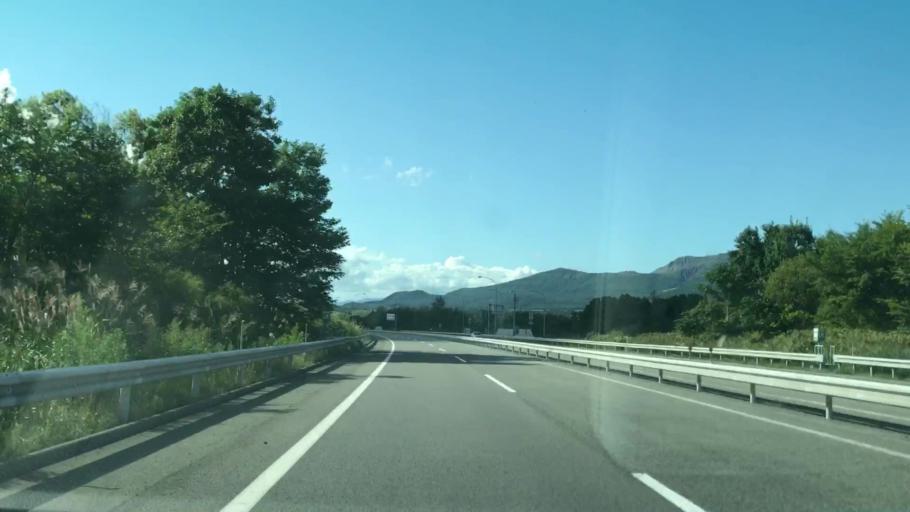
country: JP
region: Hokkaido
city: Date
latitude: 42.4844
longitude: 140.8931
